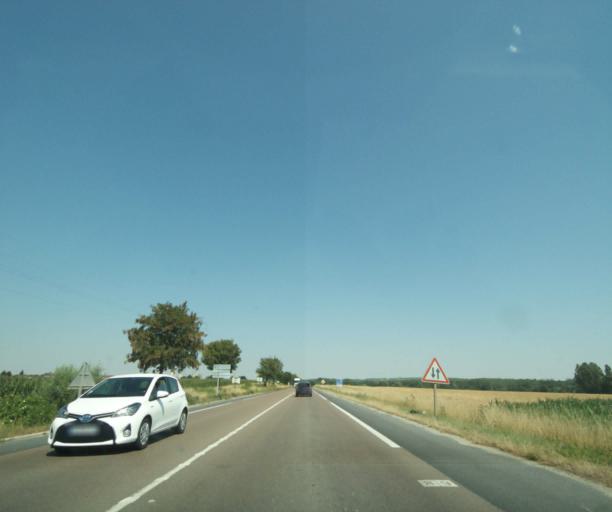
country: FR
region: Champagne-Ardenne
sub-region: Departement de la Marne
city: Frignicourt
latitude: 48.7163
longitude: 4.6345
